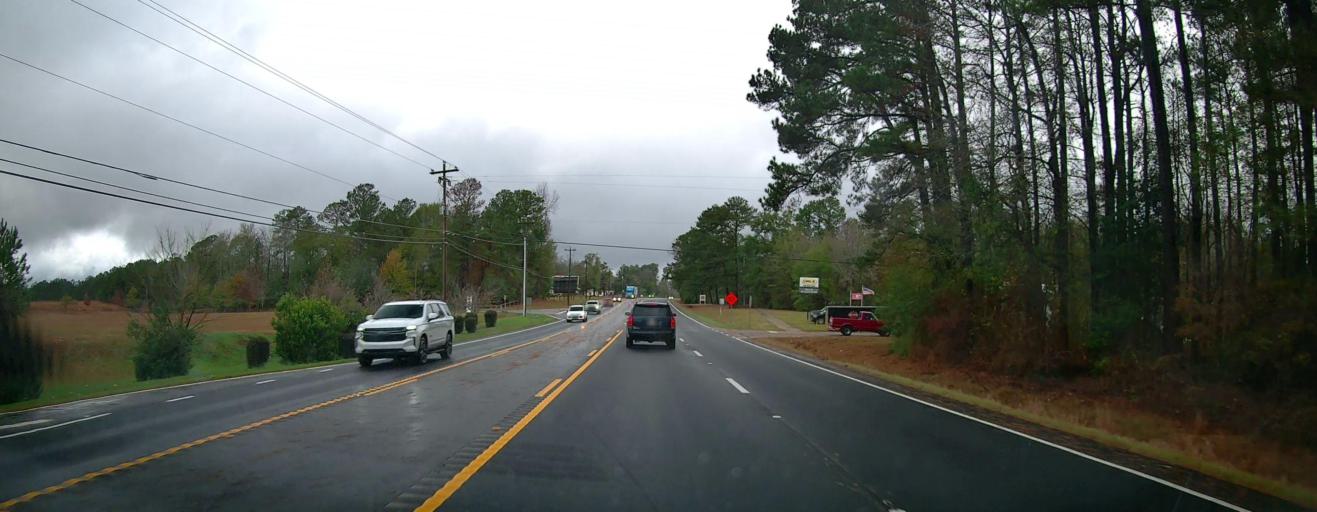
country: US
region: Georgia
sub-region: Clarke County
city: Country Club Estates
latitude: 33.9999
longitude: -83.3836
